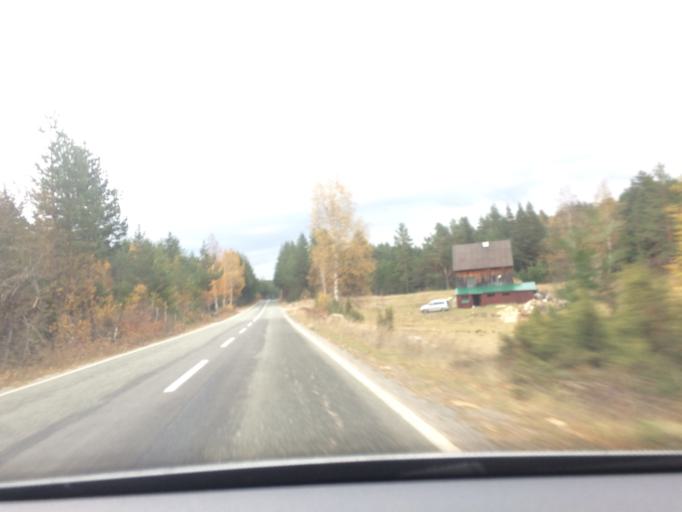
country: ME
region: Opstina Zabljak
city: Zabljak
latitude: 43.1632
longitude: 19.1945
